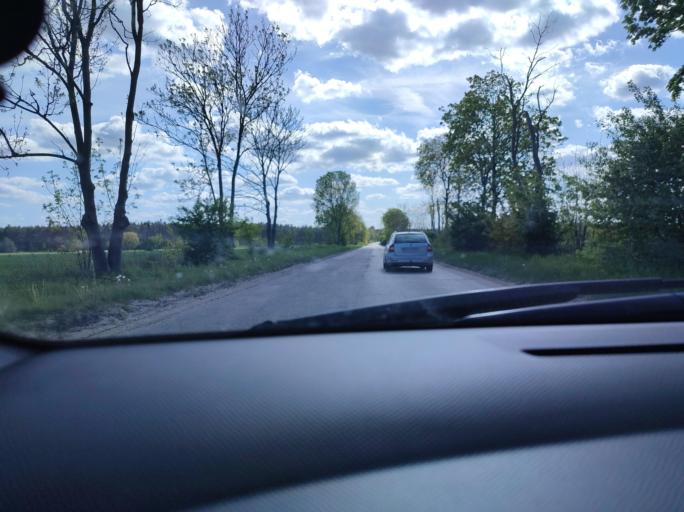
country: PL
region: West Pomeranian Voivodeship
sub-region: Powiat policki
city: Police
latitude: 53.5560
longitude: 14.5170
